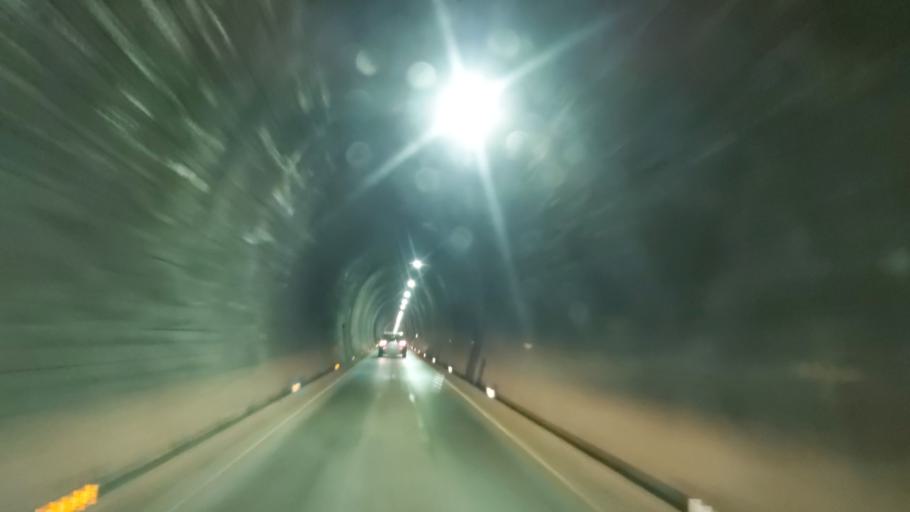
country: CL
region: Araucania
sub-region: Provincia de Cautin
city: Vilcun
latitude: -38.5211
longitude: -71.5149
